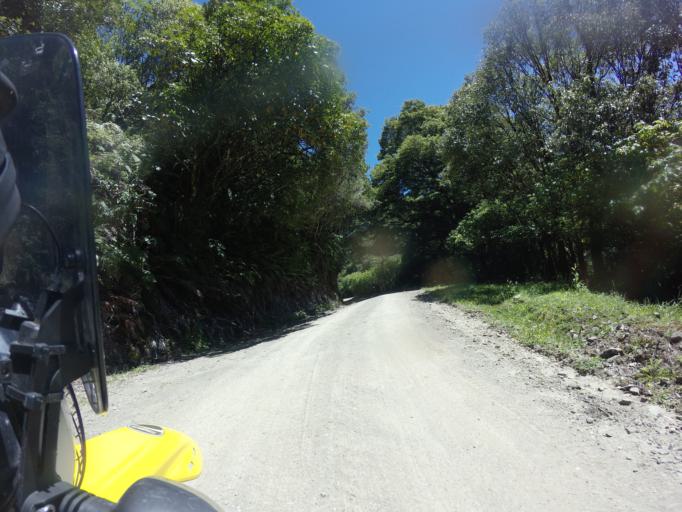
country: NZ
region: Bay of Plenty
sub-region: Opotiki District
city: Opotiki
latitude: -38.4082
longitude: 177.4212
